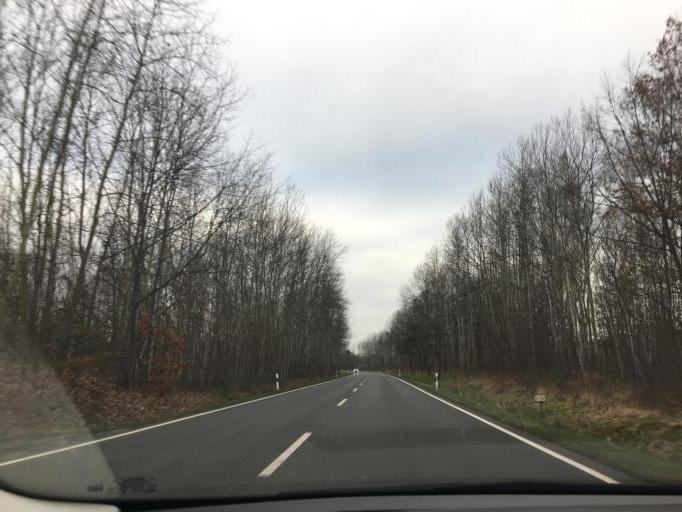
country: DE
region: Saxony
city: Kitzscher
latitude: 51.1265
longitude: 12.5574
